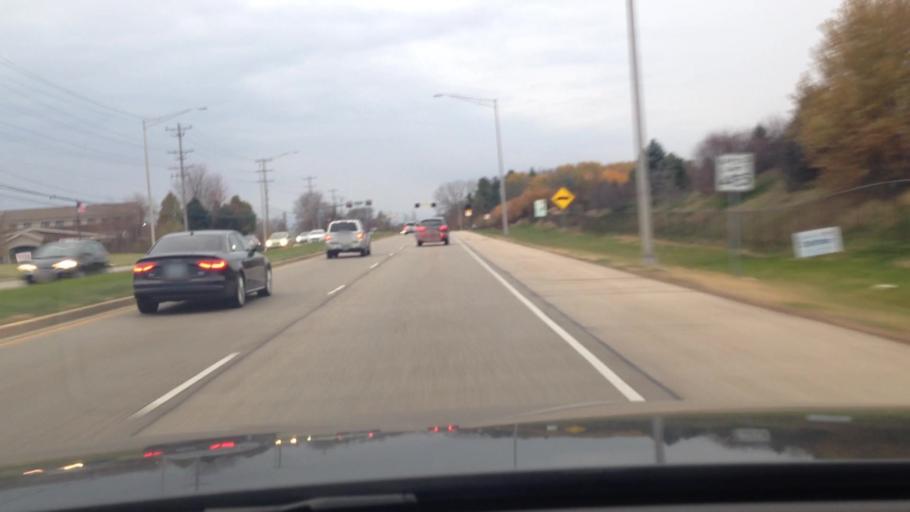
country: US
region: Illinois
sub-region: McHenry County
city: Lake in the Hills
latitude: 42.1758
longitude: -88.3695
